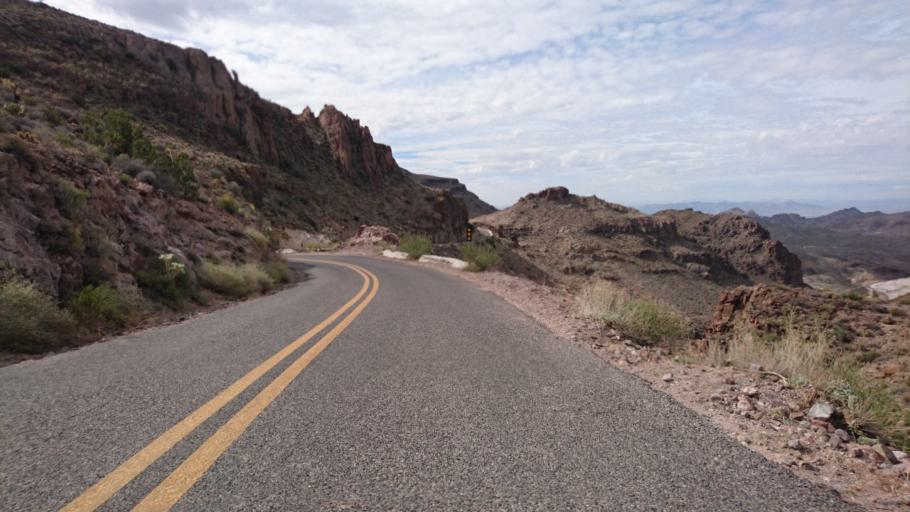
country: US
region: Arizona
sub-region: Mohave County
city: Golden Valley
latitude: 35.0456
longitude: -114.3641
